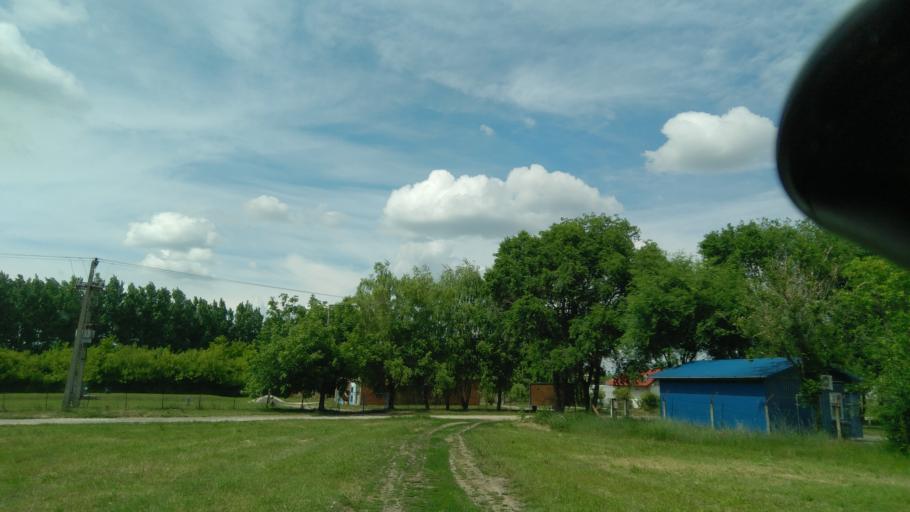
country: HU
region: Bekes
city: Mezohegyes
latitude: 46.3159
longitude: 20.8044
